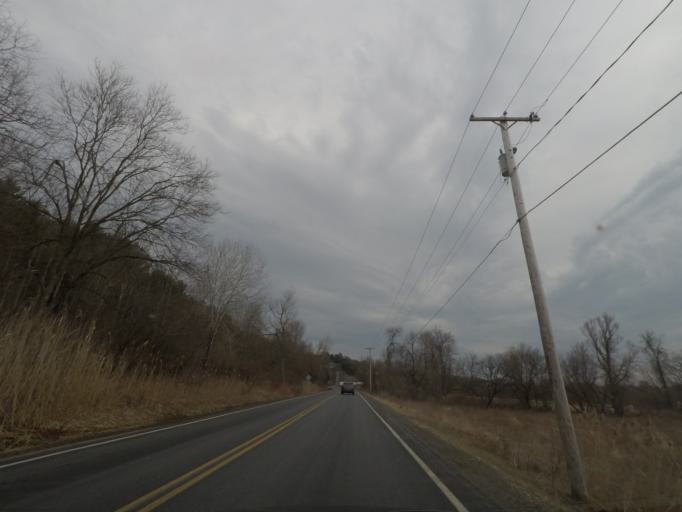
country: US
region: New York
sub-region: Saratoga County
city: Schuylerville
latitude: 43.1101
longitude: -73.5693
